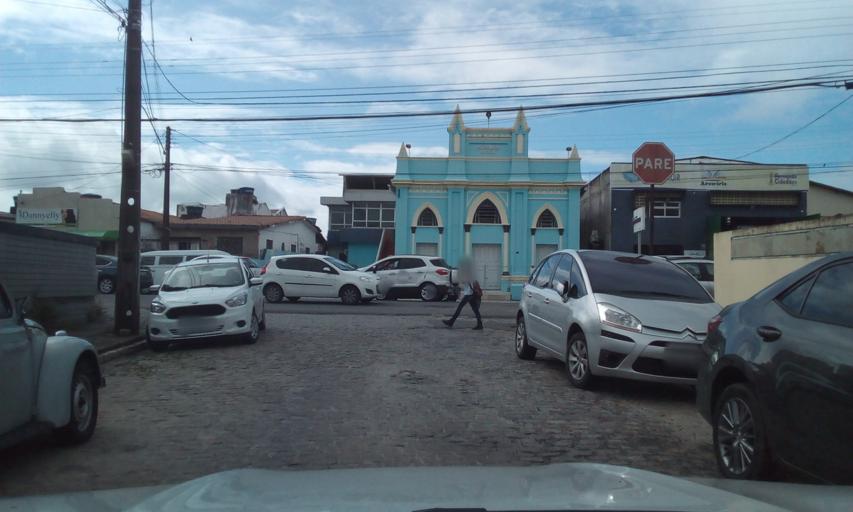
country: BR
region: Paraiba
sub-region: Joao Pessoa
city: Joao Pessoa
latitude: -7.1334
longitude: -34.8782
